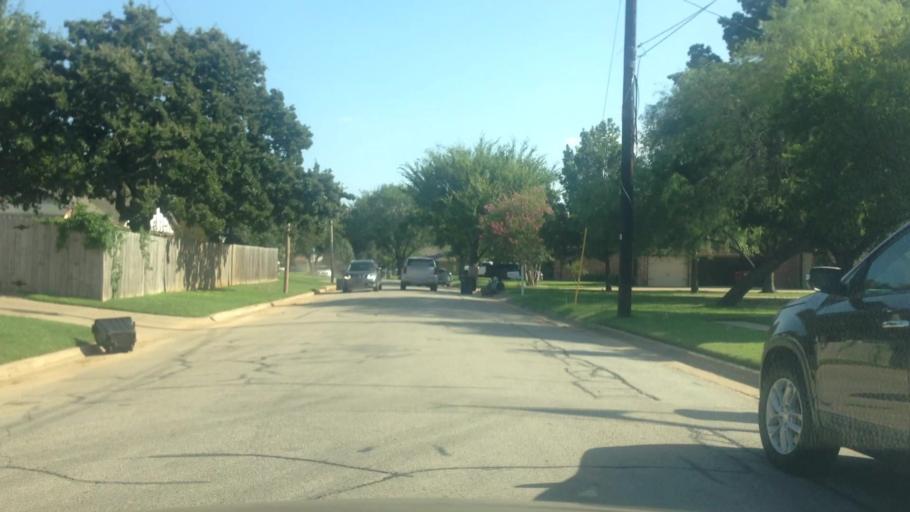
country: US
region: Texas
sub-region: Tarrant County
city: Colleyville
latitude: 32.8703
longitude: -97.1989
